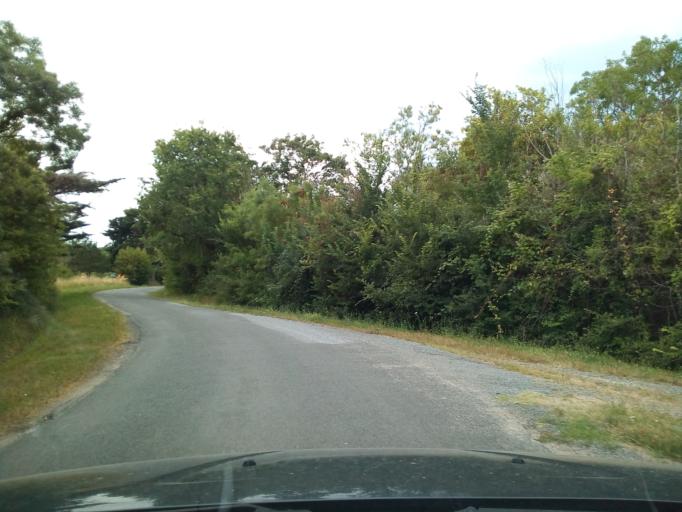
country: FR
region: Poitou-Charentes
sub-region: Departement de la Charente-Maritime
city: Dolus-d'Oleron
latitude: 45.9304
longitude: -1.2657
